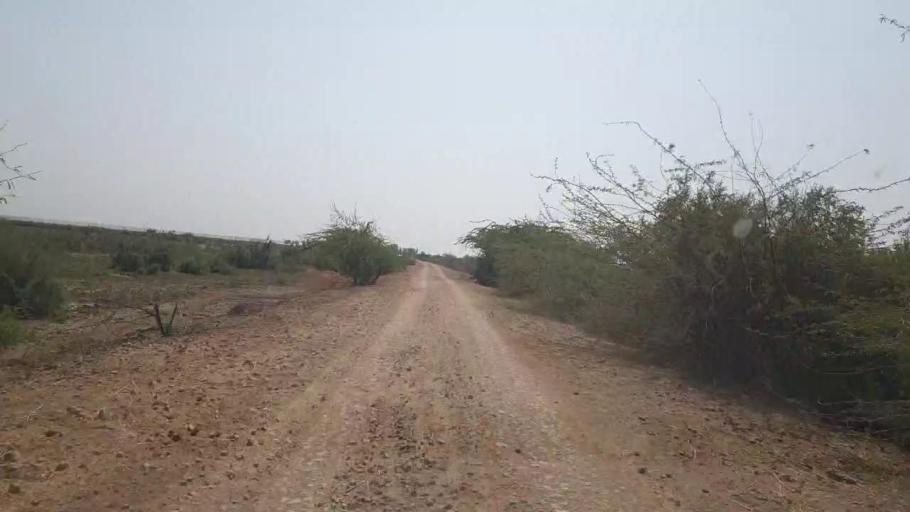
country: PK
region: Sindh
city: Jati
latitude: 24.3848
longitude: 68.5994
